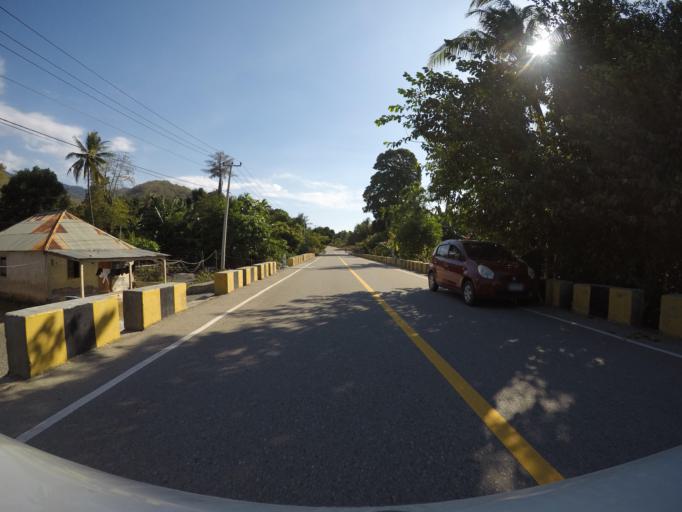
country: TL
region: Liquica
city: Maubara
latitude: -8.6196
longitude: 125.1734
